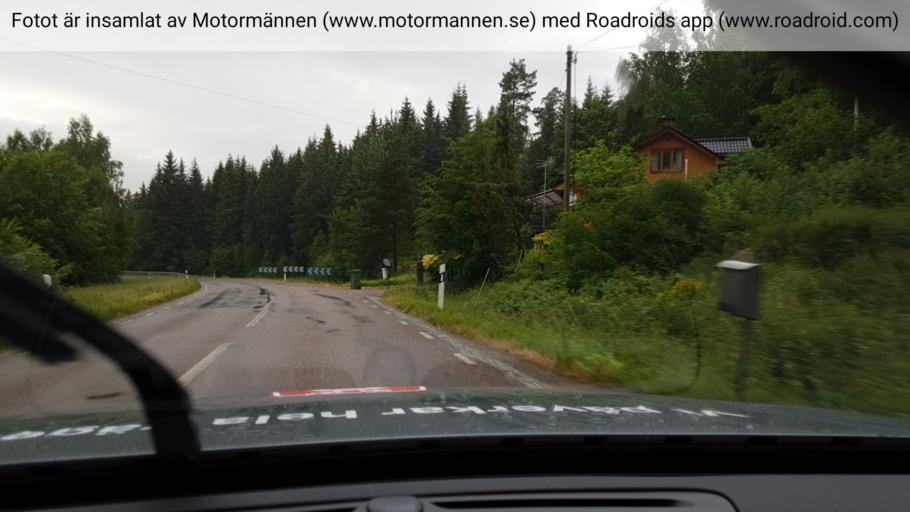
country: SE
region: Vaestmanland
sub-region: Norbergs Kommun
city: Norberg
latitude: 60.0134
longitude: 16.0525
